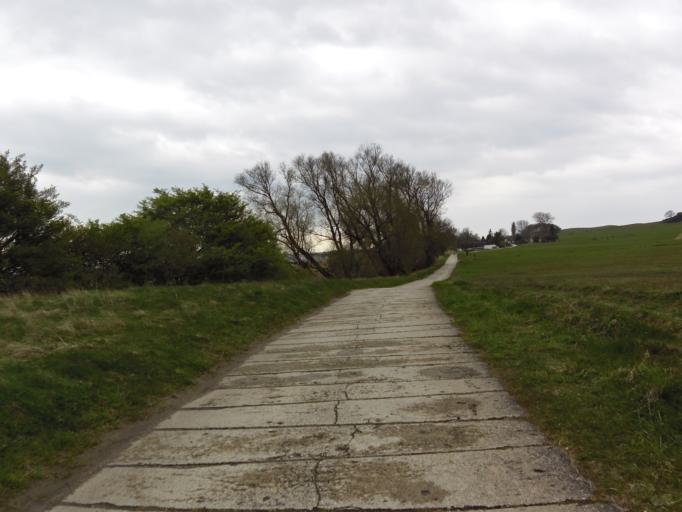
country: DE
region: Mecklenburg-Vorpommern
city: Hiddensee
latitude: 54.5955
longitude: 13.1351
